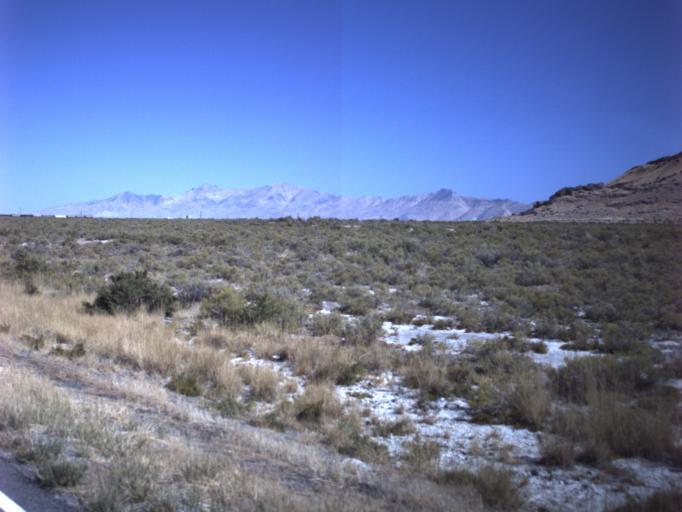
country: US
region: Utah
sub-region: Tooele County
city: Grantsville
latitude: 40.7363
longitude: -112.6558
